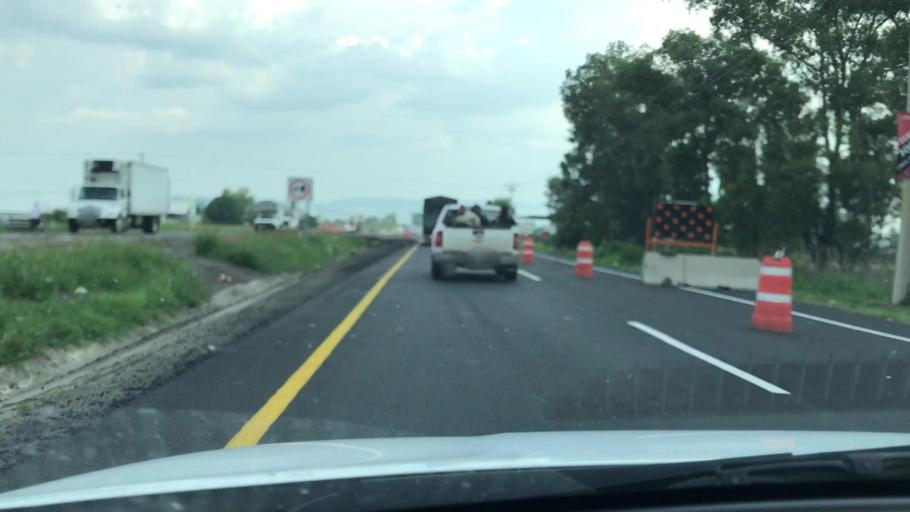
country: MX
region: Guanajuato
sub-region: Irapuato
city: San Ignacio de Rivera (Ojo de Agua)
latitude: 20.5353
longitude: -101.4586
